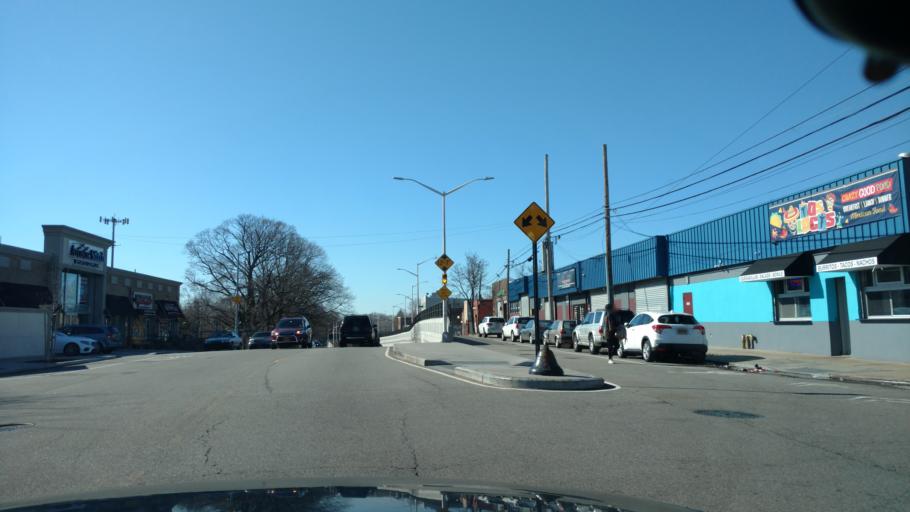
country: US
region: New York
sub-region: Kings County
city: East New York
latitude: 40.7083
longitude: -73.8722
